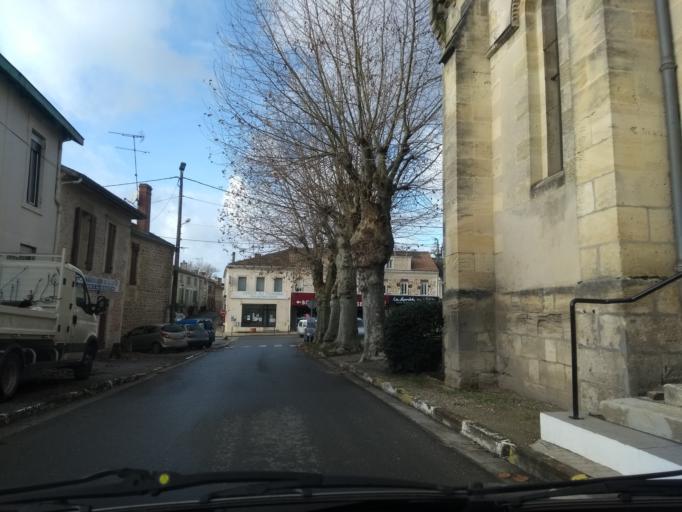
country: FR
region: Aquitaine
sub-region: Departement de la Gironde
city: Belin-Beliet
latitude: 44.4931
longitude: -0.7910
